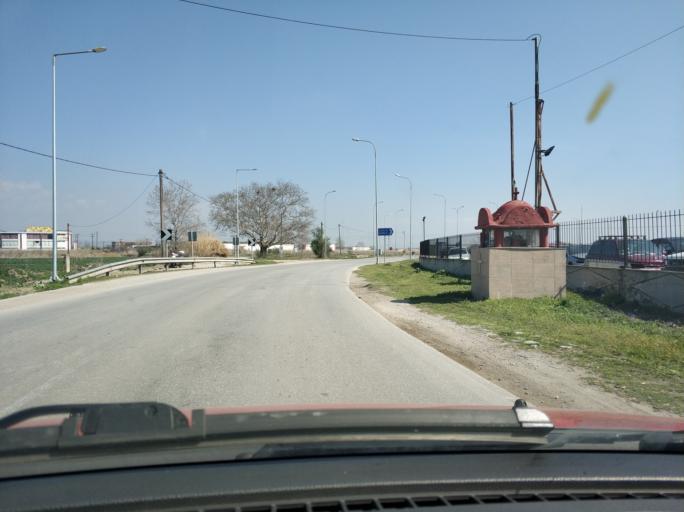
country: GR
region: Central Macedonia
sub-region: Nomos Thessalonikis
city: Lagyna
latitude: 40.7313
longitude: 23.0170
